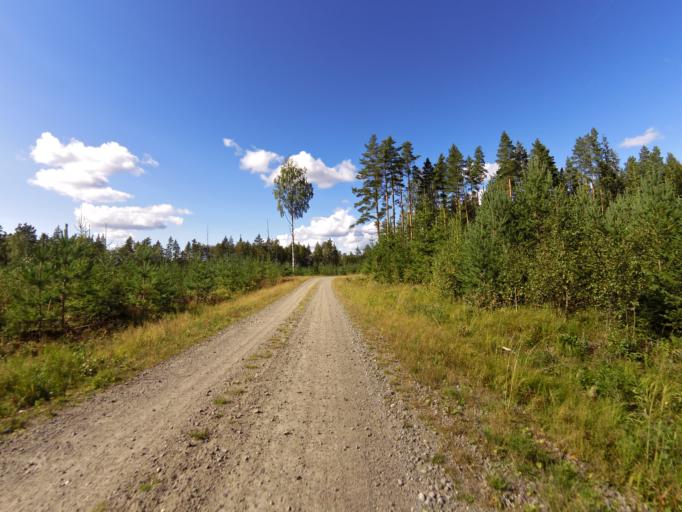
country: SE
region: Gaevleborg
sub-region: Ockelbo Kommun
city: Ockelbo
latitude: 60.8129
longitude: 16.7642
